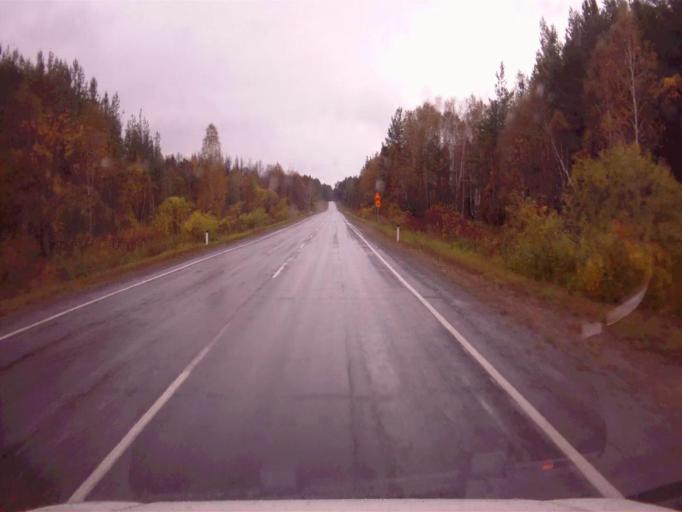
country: RU
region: Chelyabinsk
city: Verkhniy Ufaley
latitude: 56.0165
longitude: 60.3088
